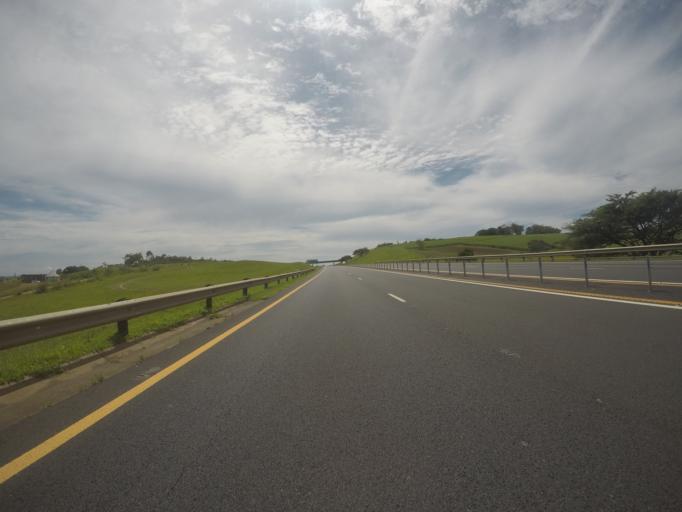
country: ZA
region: KwaZulu-Natal
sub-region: iLembe District Municipality
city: Mandeni
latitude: -29.1779
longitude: 31.5036
